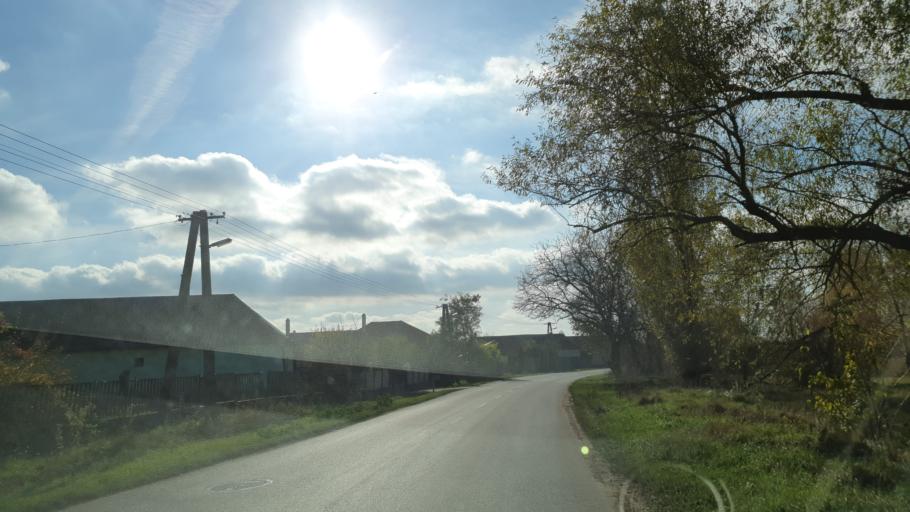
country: HU
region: Szabolcs-Szatmar-Bereg
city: Nyirkarasz
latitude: 48.1097
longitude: 22.0929
